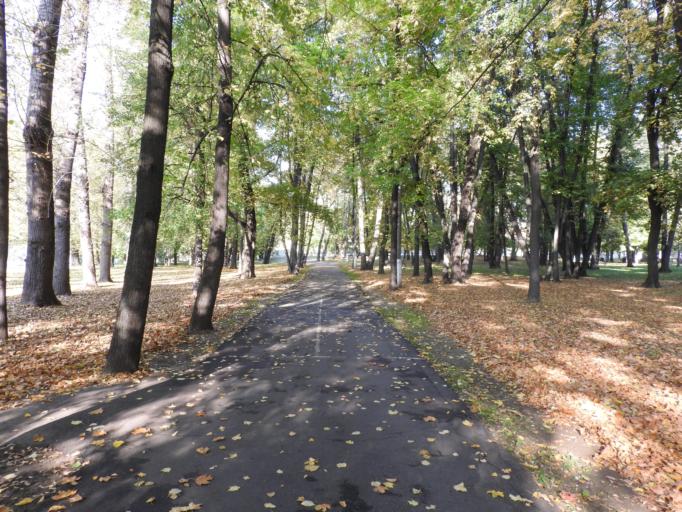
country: RU
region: Moscow
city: Lefortovo
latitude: 55.7667
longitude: 37.6927
